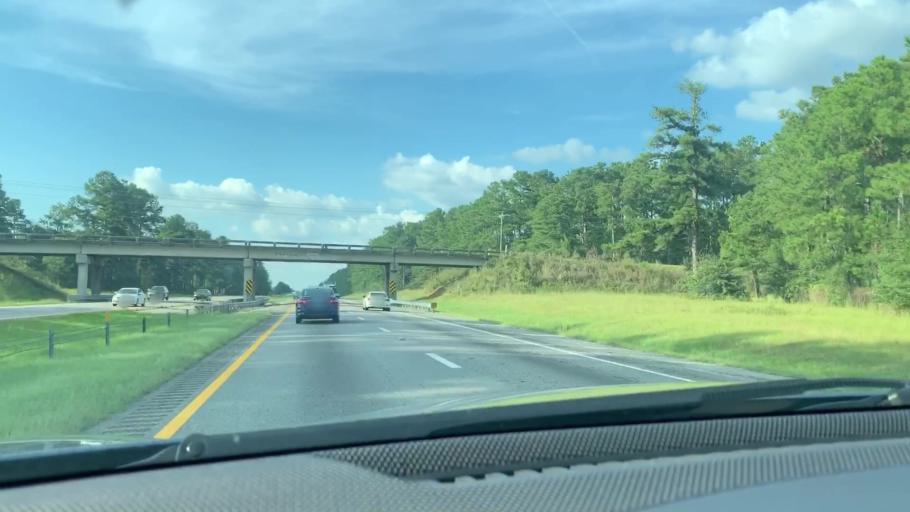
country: US
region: South Carolina
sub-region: Calhoun County
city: Saint Matthews
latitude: 33.6096
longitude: -80.8639
